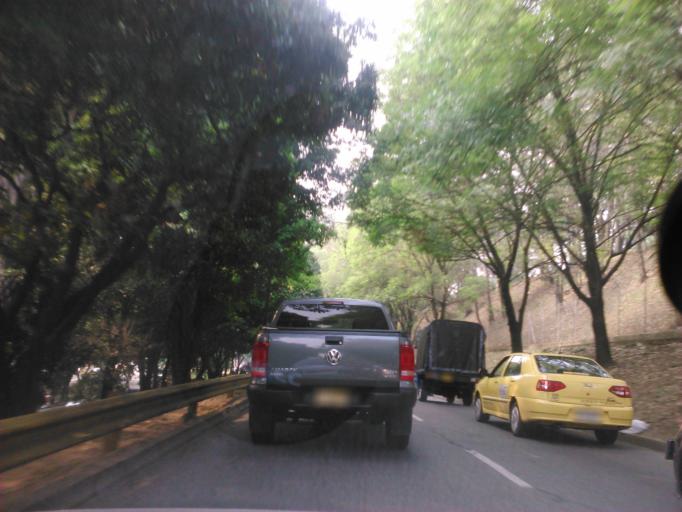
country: CO
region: Antioquia
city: Itagui
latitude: 6.2062
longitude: -75.5891
